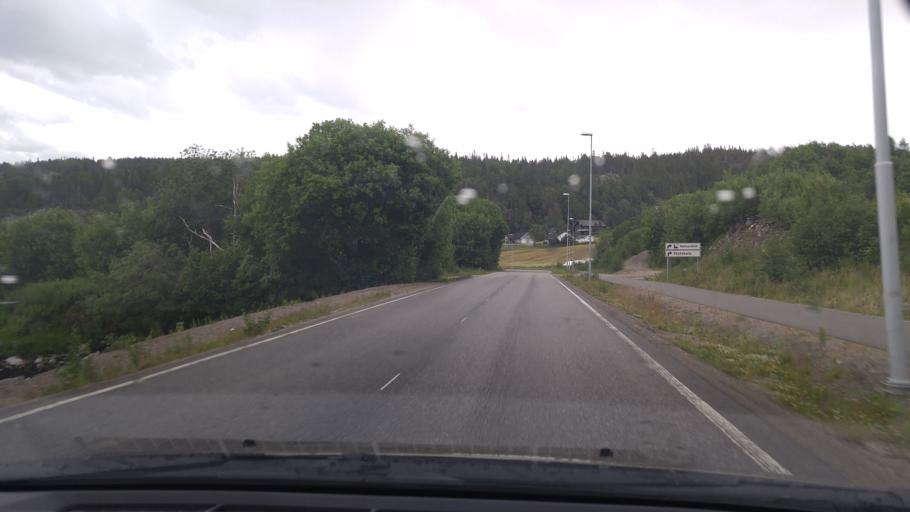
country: NO
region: Nord-Trondelag
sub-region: Namsos
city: Namsos
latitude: 64.5172
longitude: 11.5339
